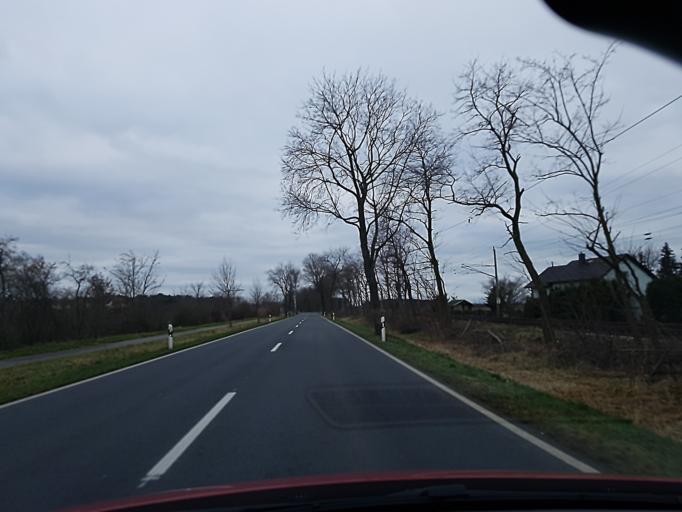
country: DE
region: Brandenburg
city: Merzdorf
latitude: 51.4193
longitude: 13.4980
